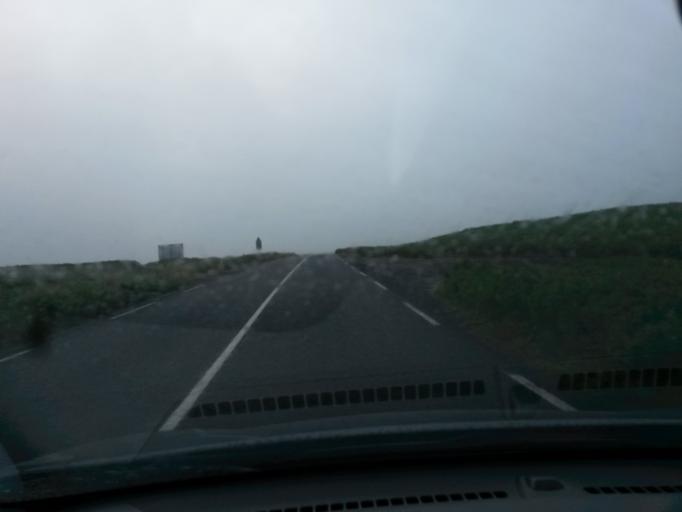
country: IS
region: South
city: Vestmannaeyjar
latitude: 63.5007
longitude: -19.4105
